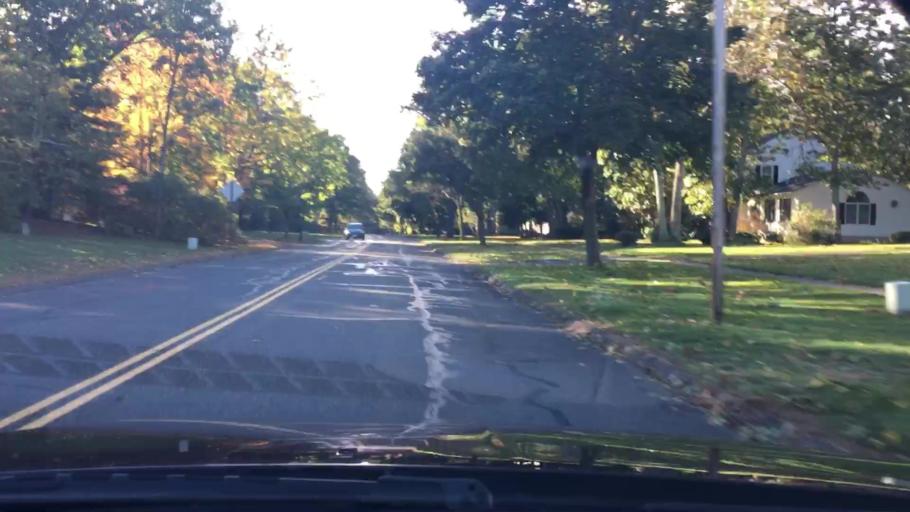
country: US
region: Connecticut
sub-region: Hartford County
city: Sherwood Manor
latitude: 42.0373
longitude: -72.5458
